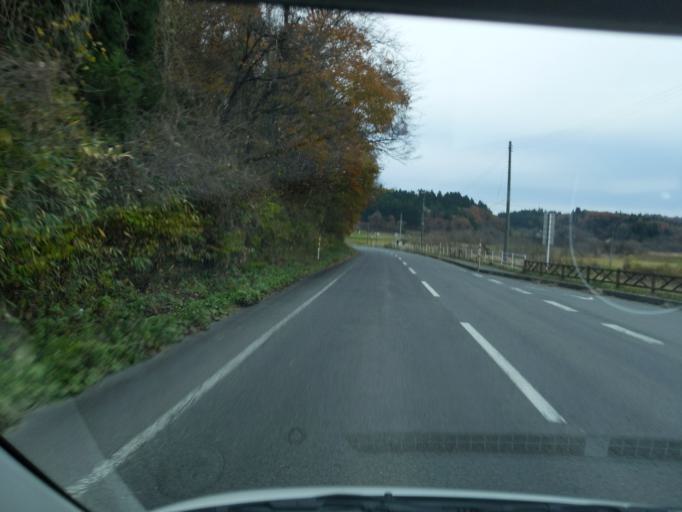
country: JP
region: Iwate
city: Kitakami
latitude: 39.2657
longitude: 141.2682
